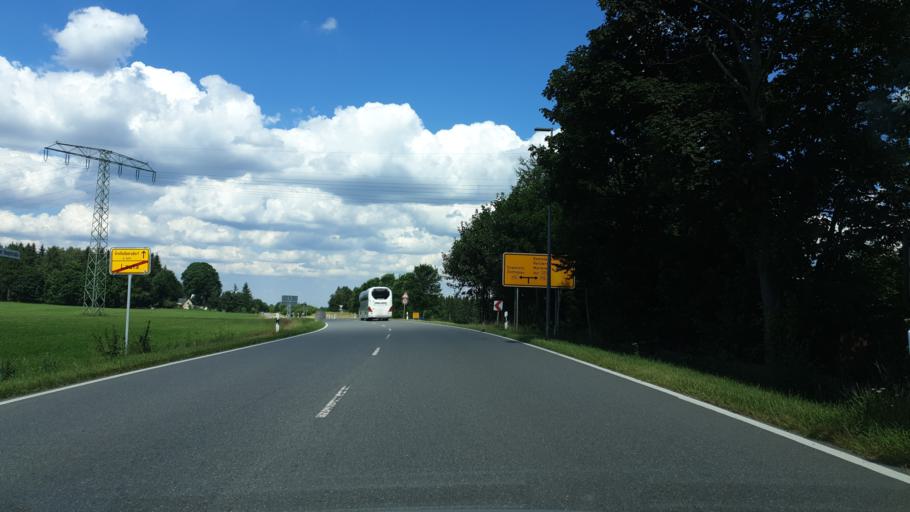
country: DE
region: Saxony
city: Marienberg
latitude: 50.6668
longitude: 13.1387
